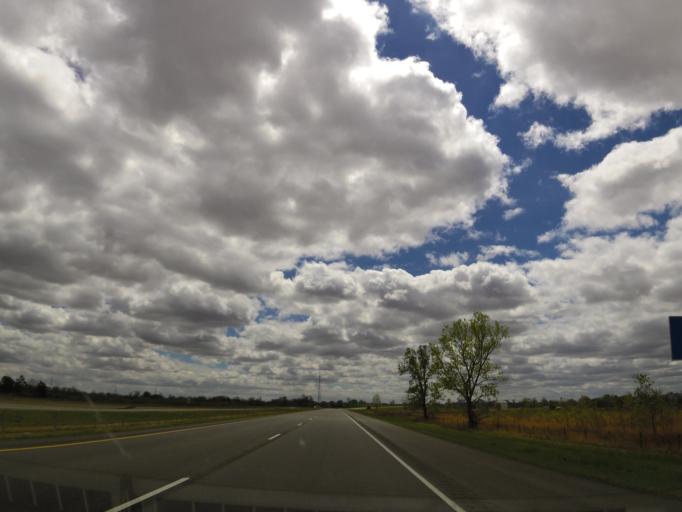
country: US
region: Arkansas
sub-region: Poinsett County
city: Marked Tree
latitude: 35.5540
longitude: -90.4969
